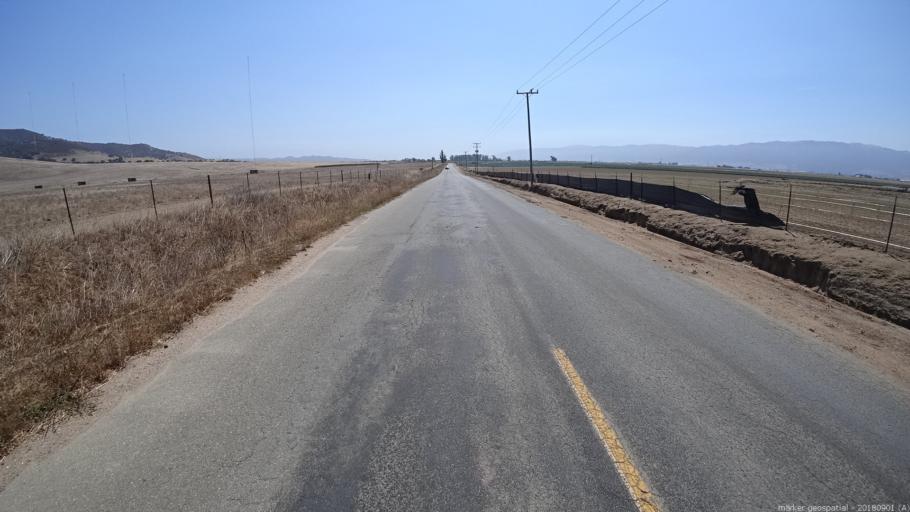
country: US
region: California
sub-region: Monterey County
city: Chualar
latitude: 36.6610
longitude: -121.5472
